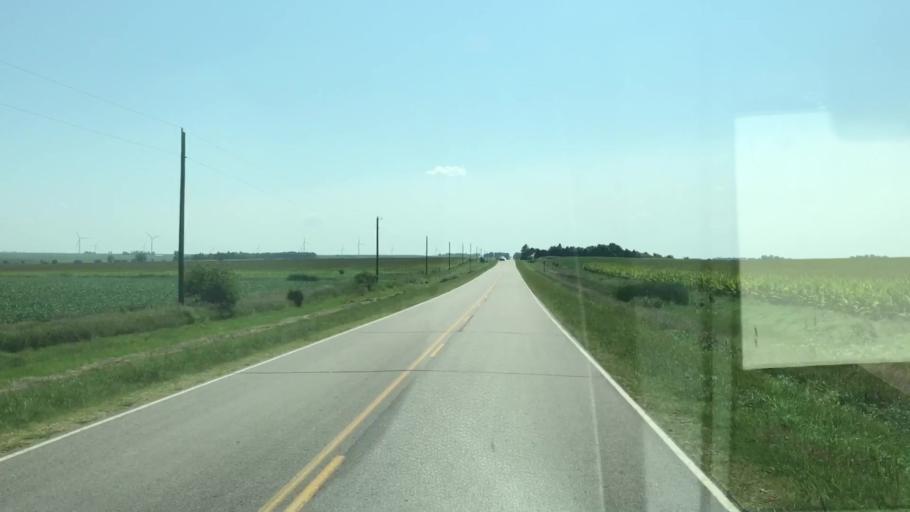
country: US
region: Iowa
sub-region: O'Brien County
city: Sanborn
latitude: 43.2569
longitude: -95.7235
